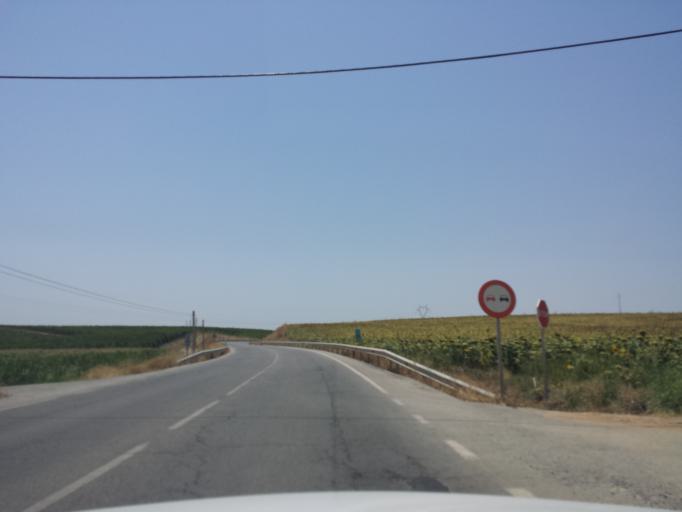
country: ES
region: Andalusia
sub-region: Provincia de Sevilla
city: Acala del Rio
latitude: 37.5336
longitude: -5.9594
